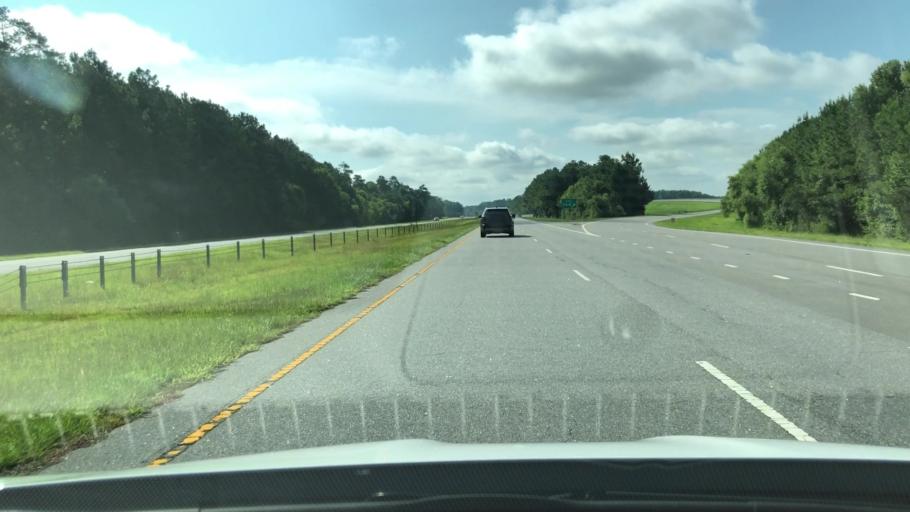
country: US
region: North Carolina
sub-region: Pasquotank County
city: Elizabeth City
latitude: 36.3835
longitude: -76.3148
